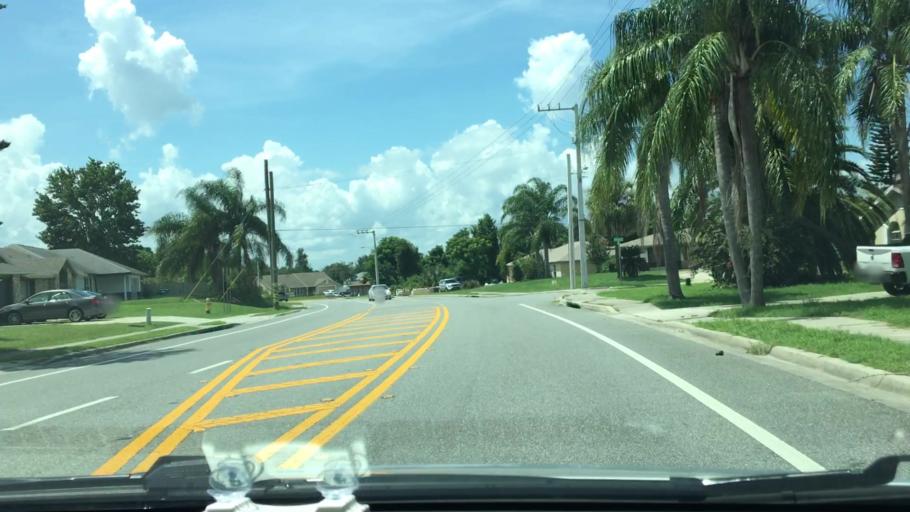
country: US
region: Florida
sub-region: Volusia County
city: Deltona
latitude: 28.8882
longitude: -81.2102
